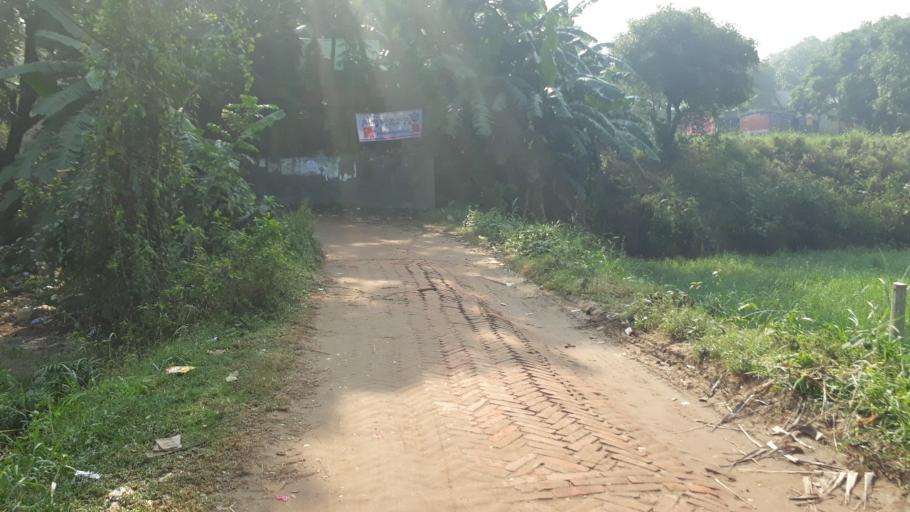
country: BD
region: Dhaka
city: Tungi
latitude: 23.8804
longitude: 90.2584
